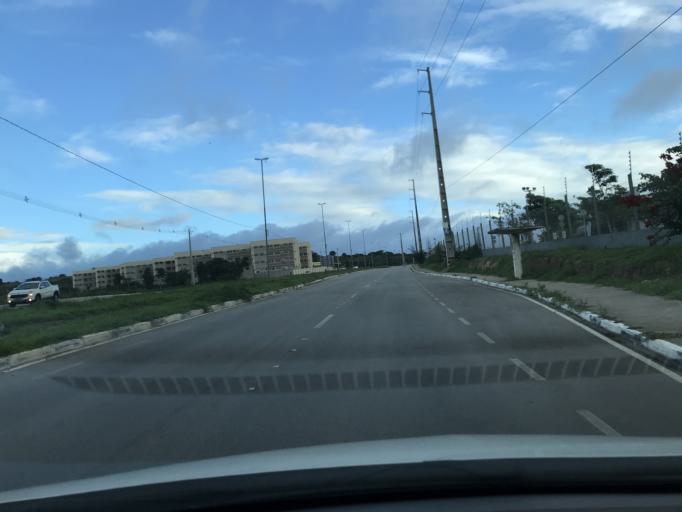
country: BR
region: Pernambuco
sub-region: Caruaru
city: Caruaru
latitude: -8.3000
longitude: -35.9396
